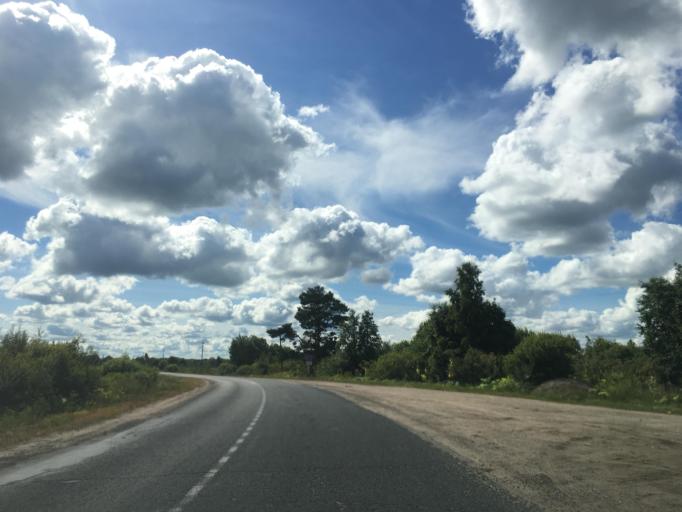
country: RU
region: Pskov
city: Pskov
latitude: 57.7365
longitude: 28.1545
